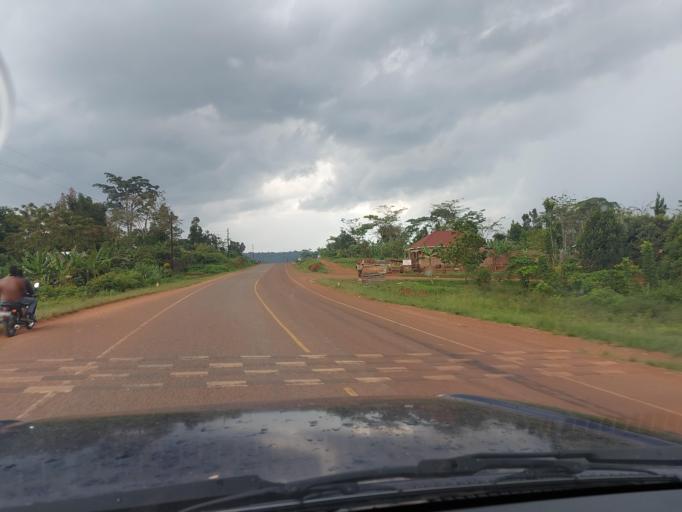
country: UG
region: Central Region
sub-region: Mukono District
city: Mukono
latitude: 0.2651
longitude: 32.8408
